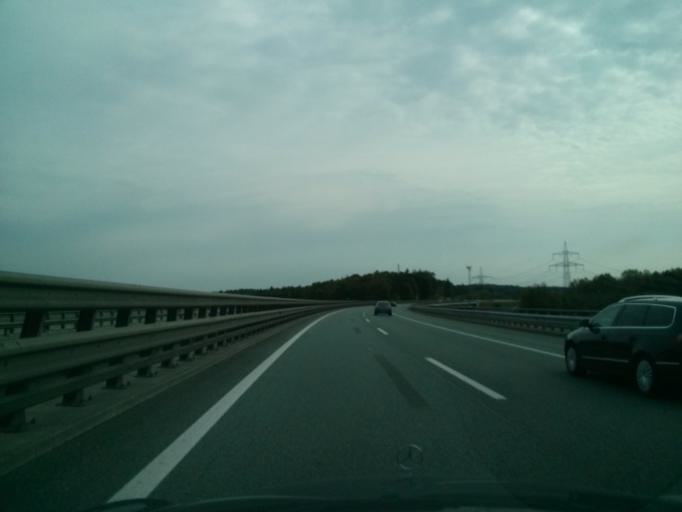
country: AT
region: Styria
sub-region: Politischer Bezirk Weiz
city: Nitscha
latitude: 47.1039
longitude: 15.7592
